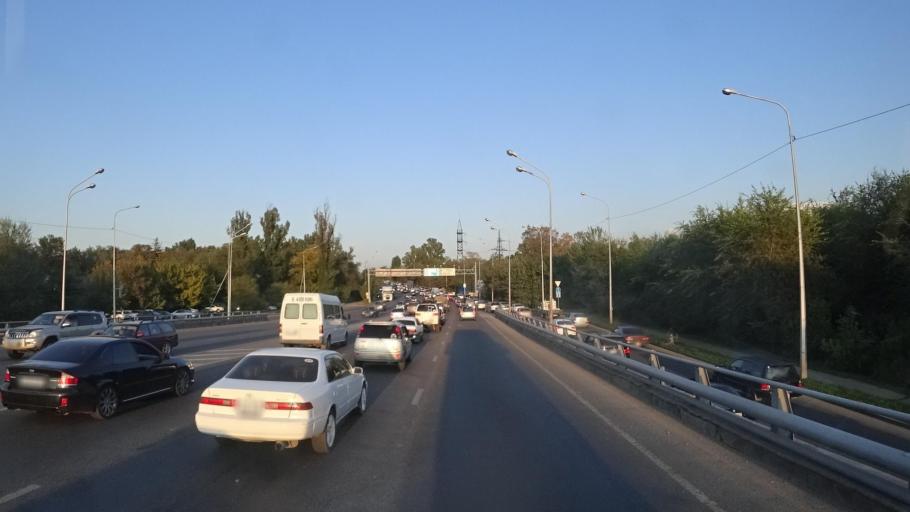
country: KZ
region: Almaty Qalasy
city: Almaty
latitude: 43.2932
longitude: 76.9426
